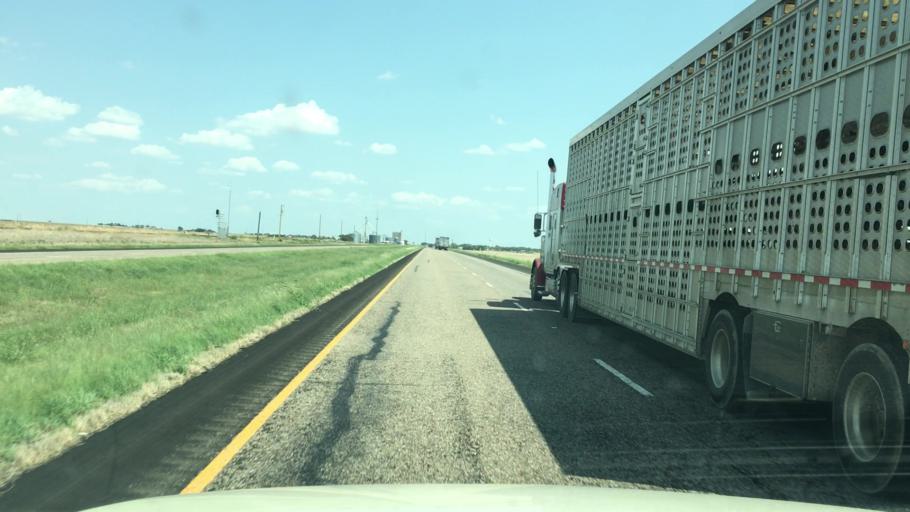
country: US
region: Texas
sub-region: Armstrong County
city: Claude
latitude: 35.1233
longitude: -101.3916
